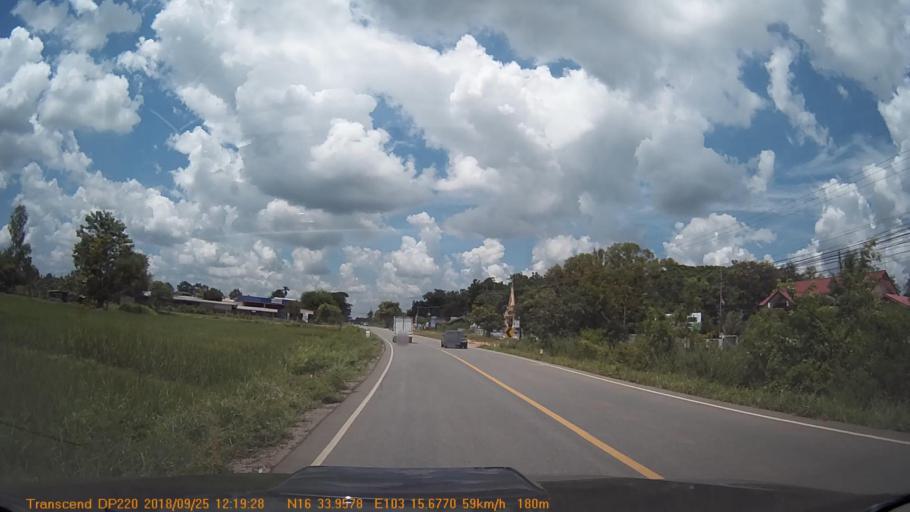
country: TH
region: Kalasin
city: Huai Mek
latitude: 16.5659
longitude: 103.2613
